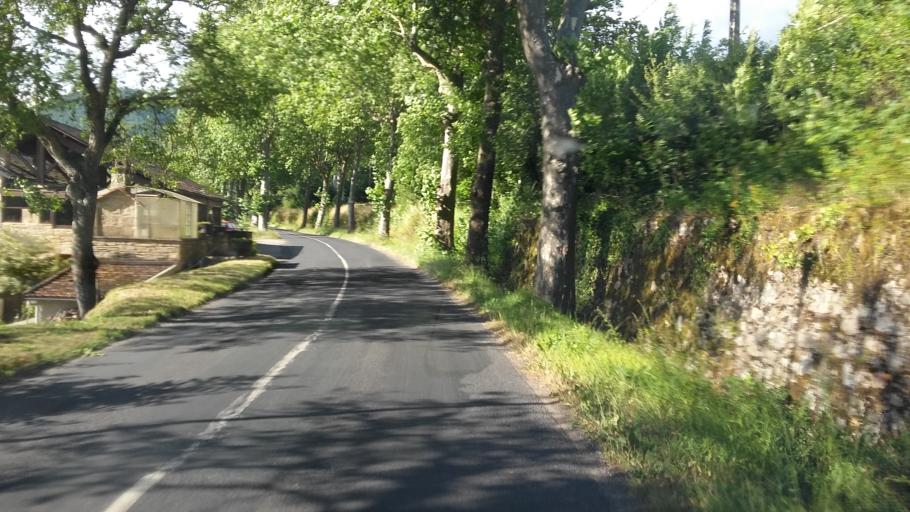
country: FR
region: Languedoc-Roussillon
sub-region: Departement de la Lozere
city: Meyrueis
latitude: 44.0218
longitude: 3.3531
